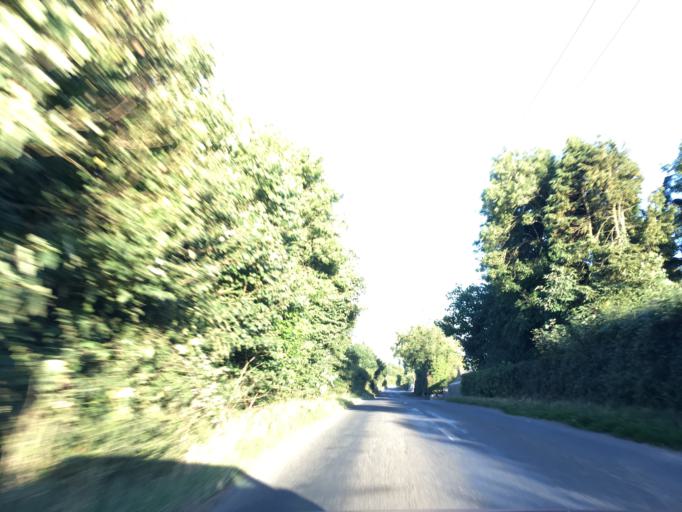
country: IE
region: Munster
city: Cashel
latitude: 52.4833
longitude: -7.9388
